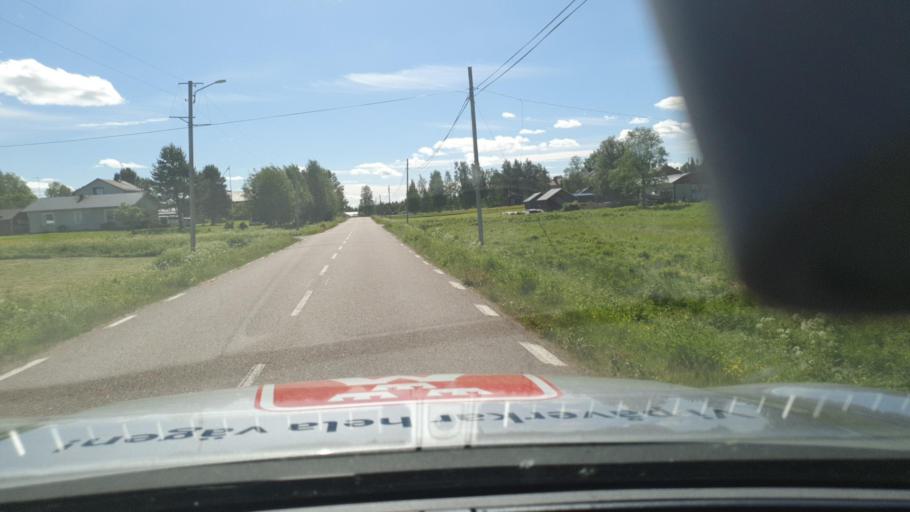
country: SE
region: Norrbotten
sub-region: Overkalix Kommun
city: OEverkalix
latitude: 67.0056
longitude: 22.4900
